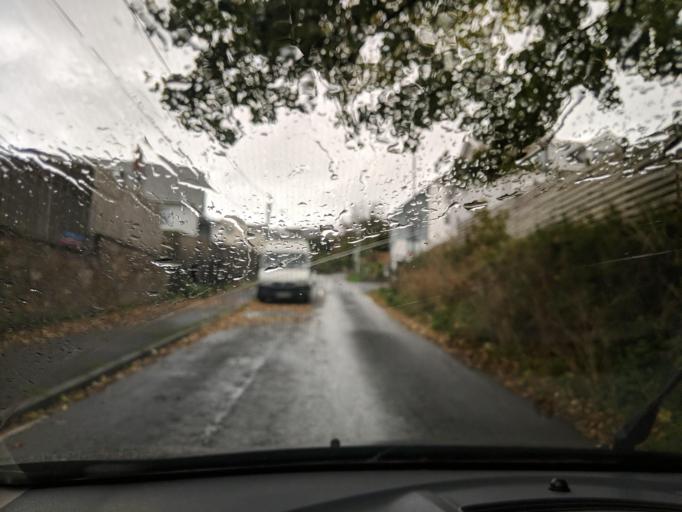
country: GB
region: England
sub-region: Cornwall
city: Wadebridge
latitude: 50.5154
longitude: -4.8214
